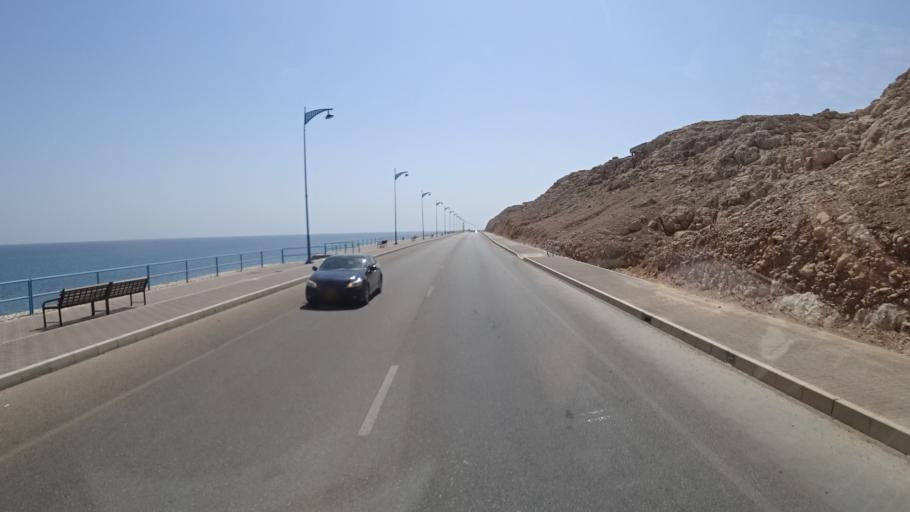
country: OM
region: Ash Sharqiyah
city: Sur
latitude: 22.5661
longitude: 59.5660
